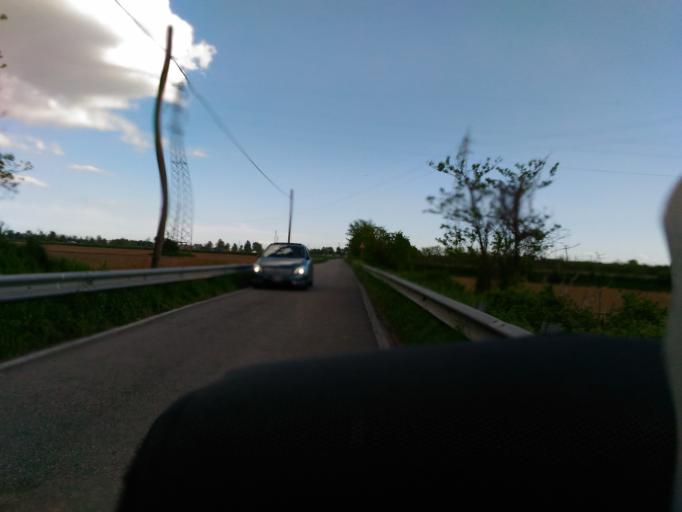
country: IT
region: Lombardy
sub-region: Citta metropolitana di Milano
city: Triginto
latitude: 45.3979
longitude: 9.3192
